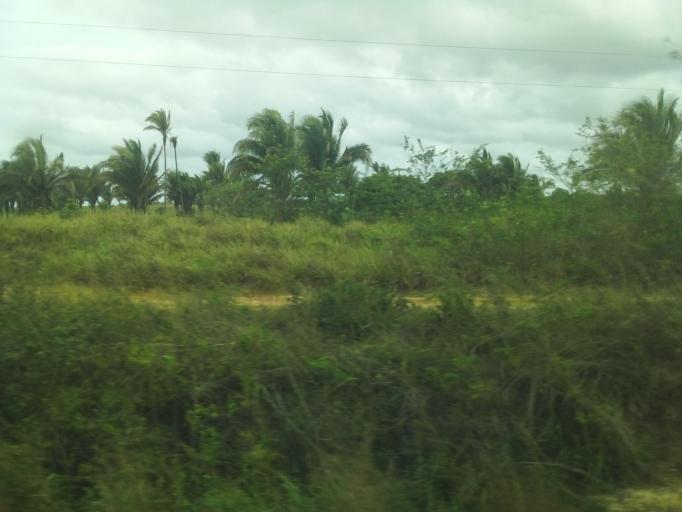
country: BR
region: Maranhao
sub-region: Itapecuru Mirim
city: Itapecuru Mirim
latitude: -3.2171
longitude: -44.4039
